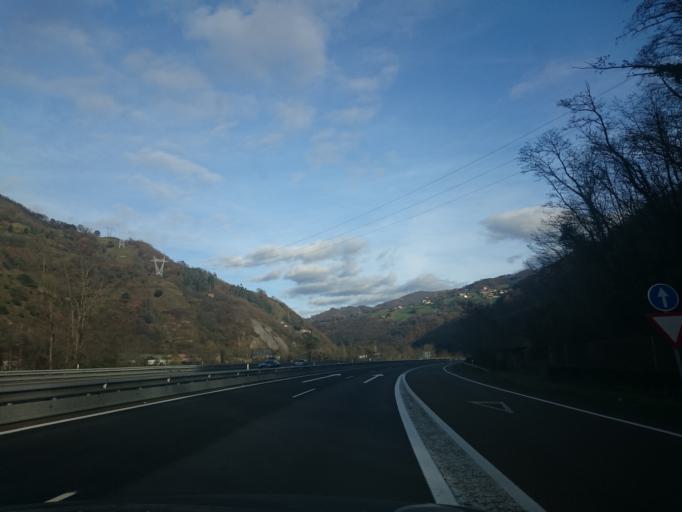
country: ES
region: Asturias
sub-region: Province of Asturias
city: Pola de Lena
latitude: 43.1841
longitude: -5.8072
